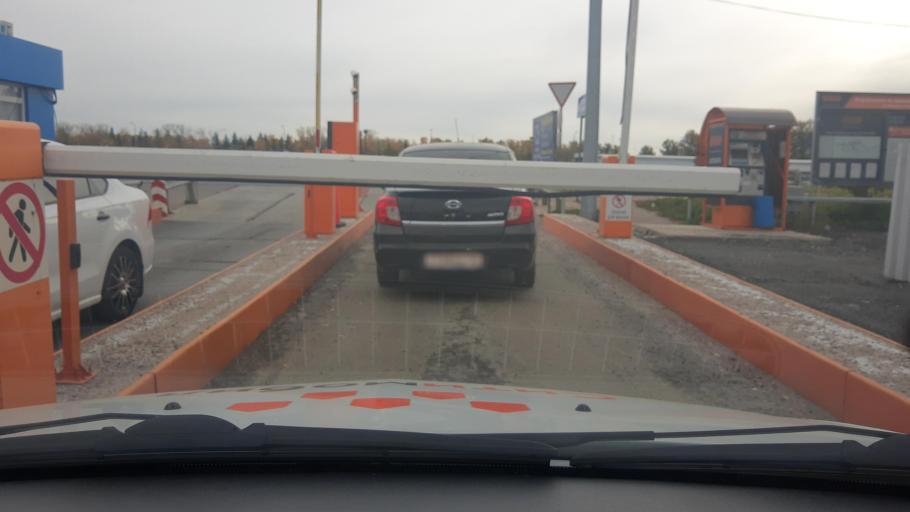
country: RU
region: Bashkortostan
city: Ufa
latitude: 54.5699
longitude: 55.8866
